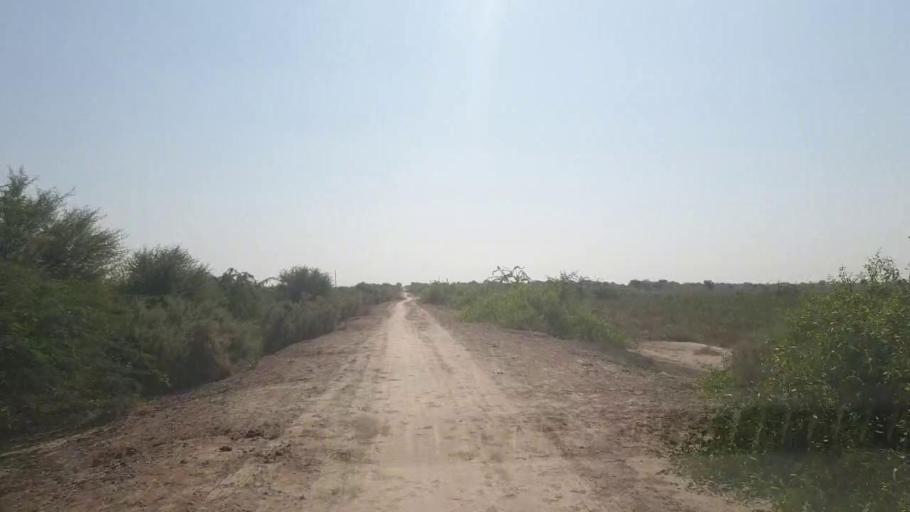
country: PK
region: Sindh
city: Tando Bago
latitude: 24.8965
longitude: 69.1645
